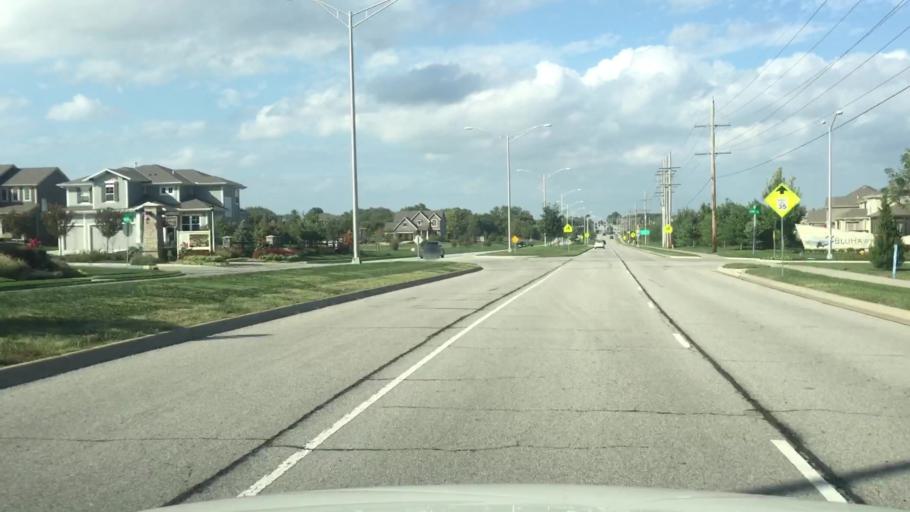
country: US
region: Kansas
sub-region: Johnson County
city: Lenexa
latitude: 38.8278
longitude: -94.6863
